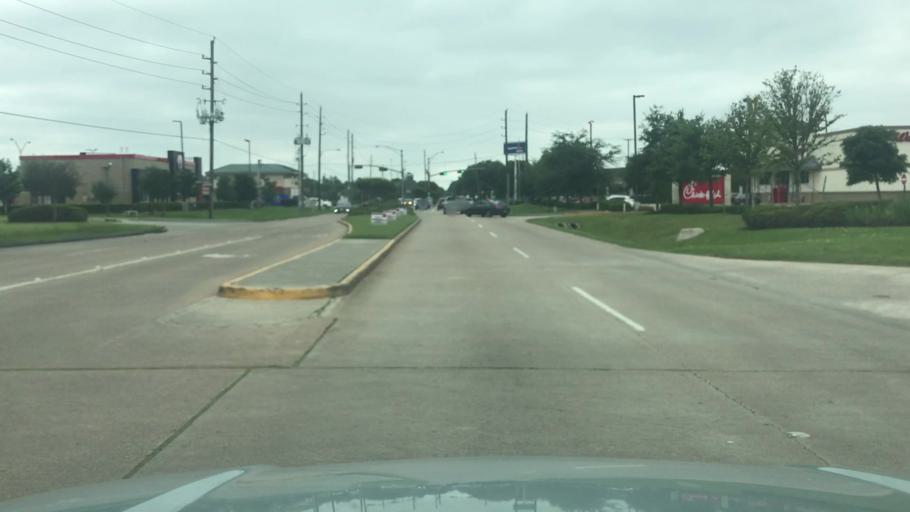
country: US
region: Texas
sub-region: Harris County
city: Katy
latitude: 29.7745
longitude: -95.8188
